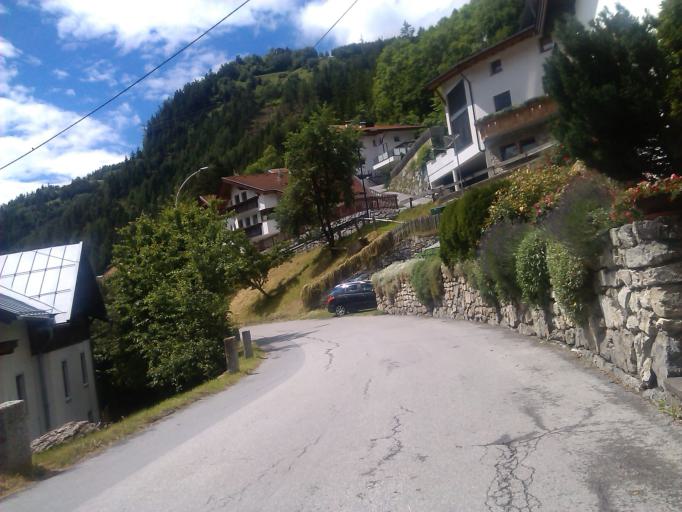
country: AT
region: Tyrol
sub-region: Politischer Bezirk Landeck
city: Prutz
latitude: 47.0835
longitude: 10.6606
